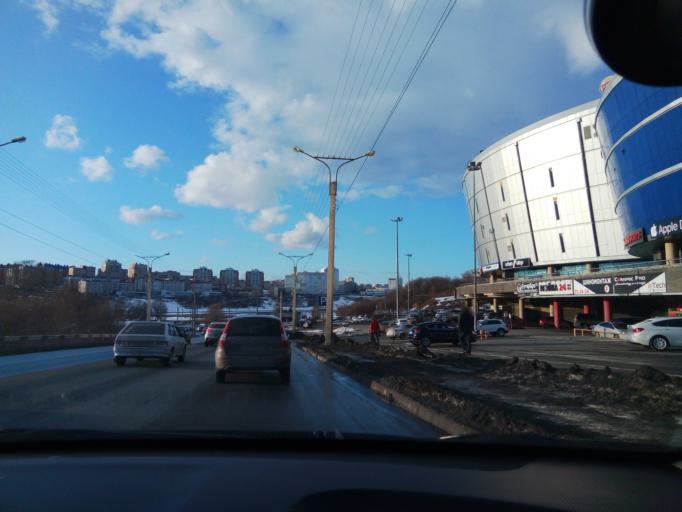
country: RU
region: Chuvashia
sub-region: Cheboksarskiy Rayon
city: Cheboksary
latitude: 56.1346
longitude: 47.2398
